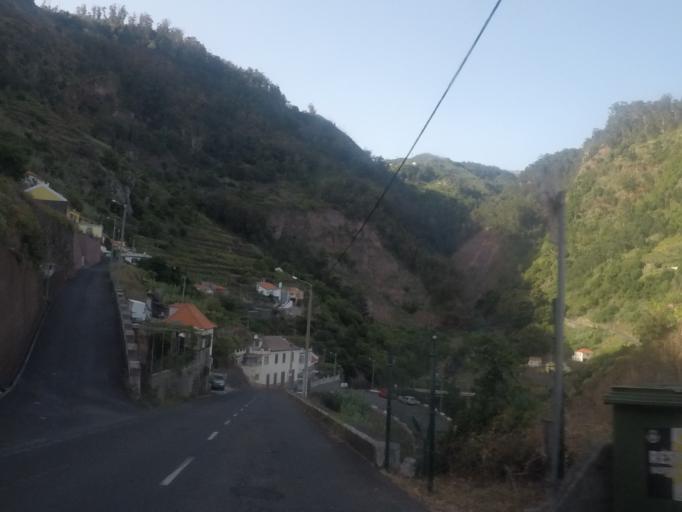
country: PT
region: Madeira
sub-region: Calheta
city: Arco da Calheta
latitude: 32.7114
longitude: -17.1352
